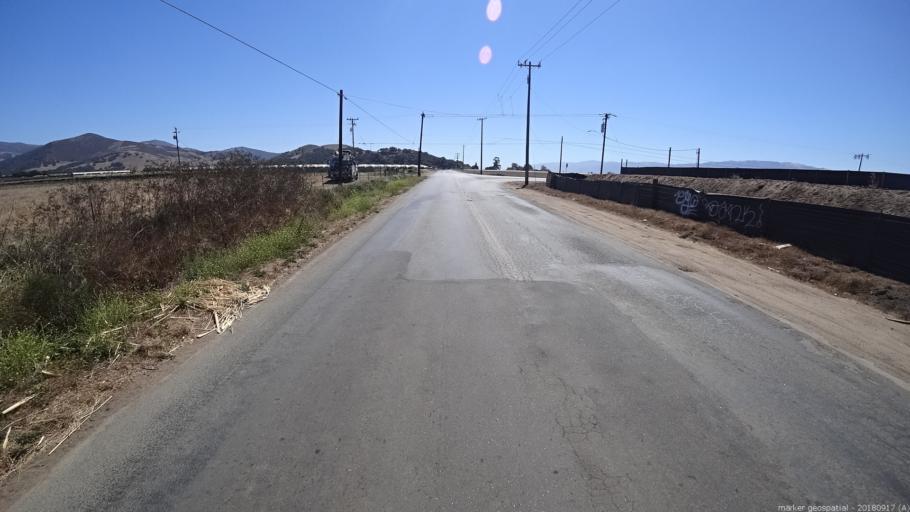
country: US
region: California
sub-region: Monterey County
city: Salinas
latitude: 36.6990
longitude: -121.5745
